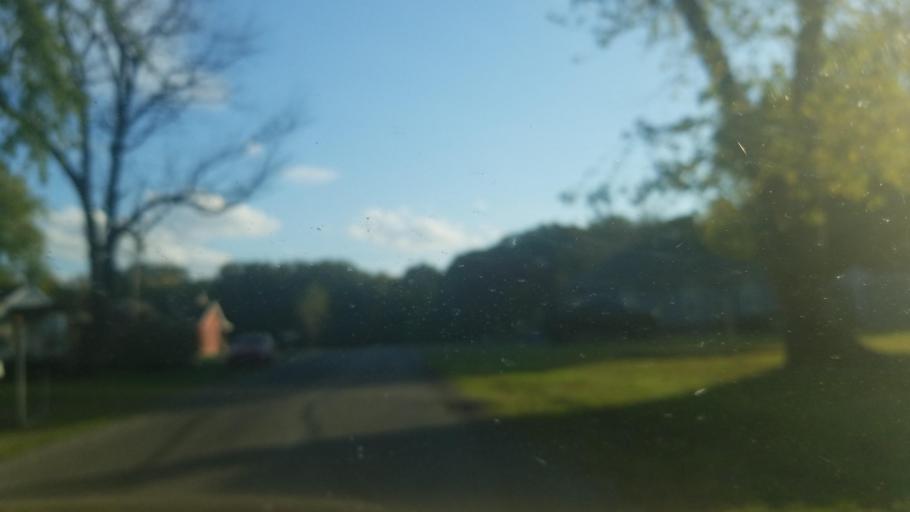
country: US
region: Illinois
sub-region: Williamson County
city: Marion
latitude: 37.7625
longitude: -88.8070
